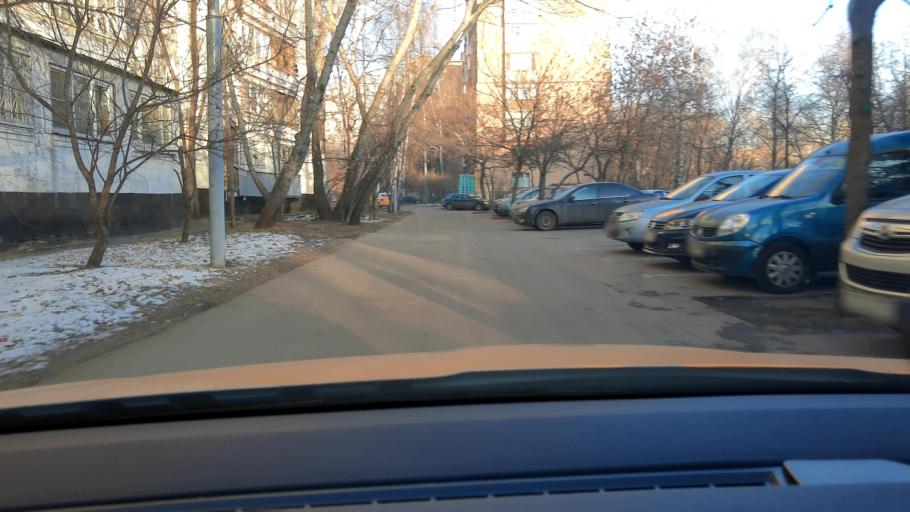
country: RU
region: Moscow
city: Lyublino
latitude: 55.6659
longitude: 37.7442
